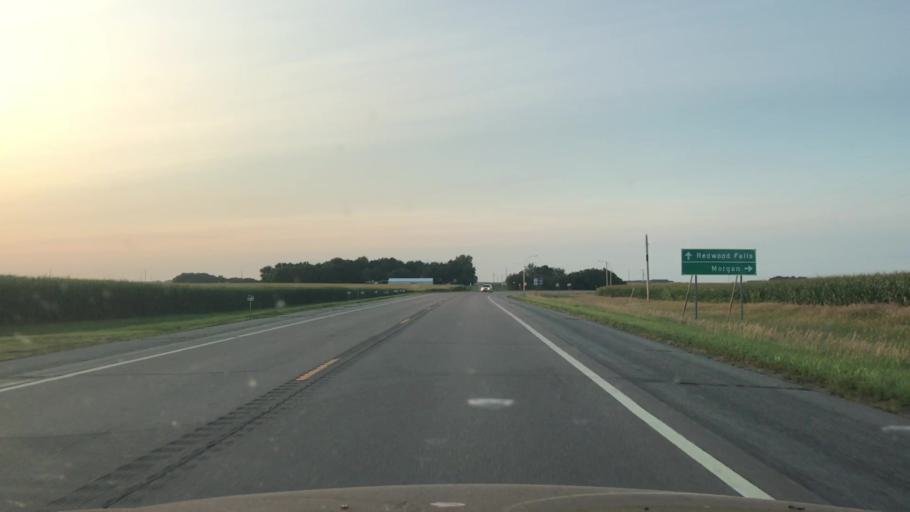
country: US
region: Minnesota
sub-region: Redwood County
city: Redwood Falls
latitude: 44.4102
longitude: -95.1276
